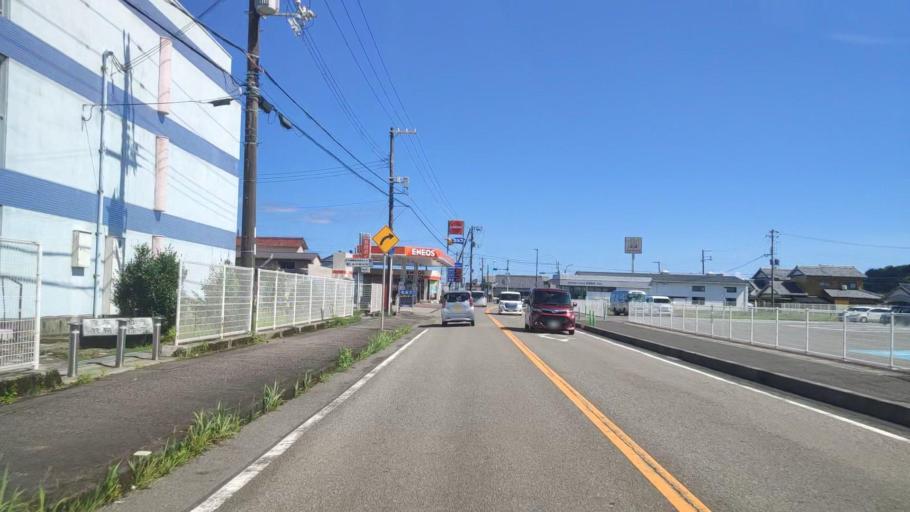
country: JP
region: Wakayama
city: Shingu
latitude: 33.5831
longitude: 135.9199
